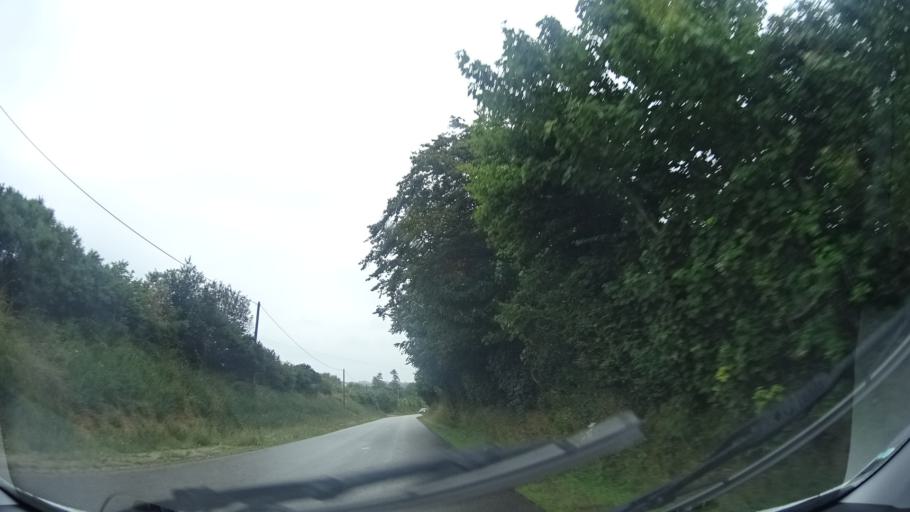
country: FR
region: Lower Normandy
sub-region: Departement de la Manche
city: Urville-Nacqueville
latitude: 49.5957
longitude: -1.7601
